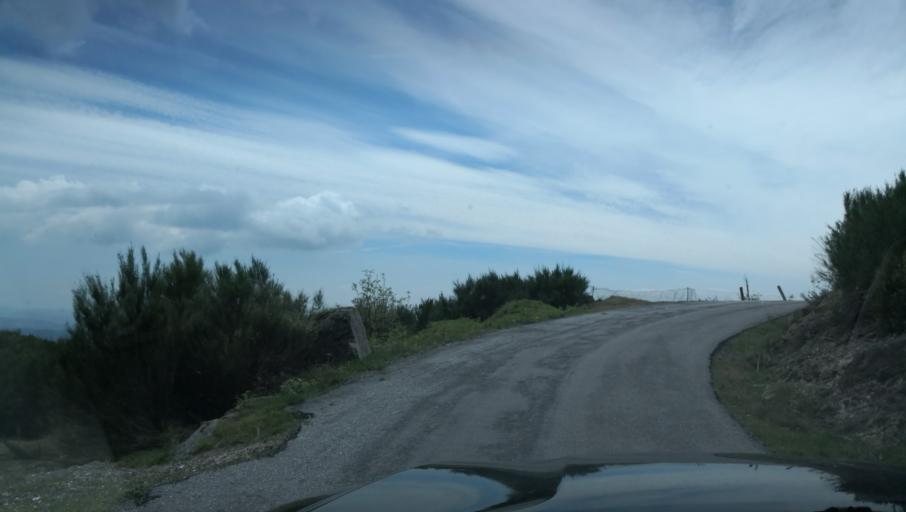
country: PT
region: Vila Real
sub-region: Vila Real
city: Vila Real
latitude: 41.3018
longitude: -7.8109
